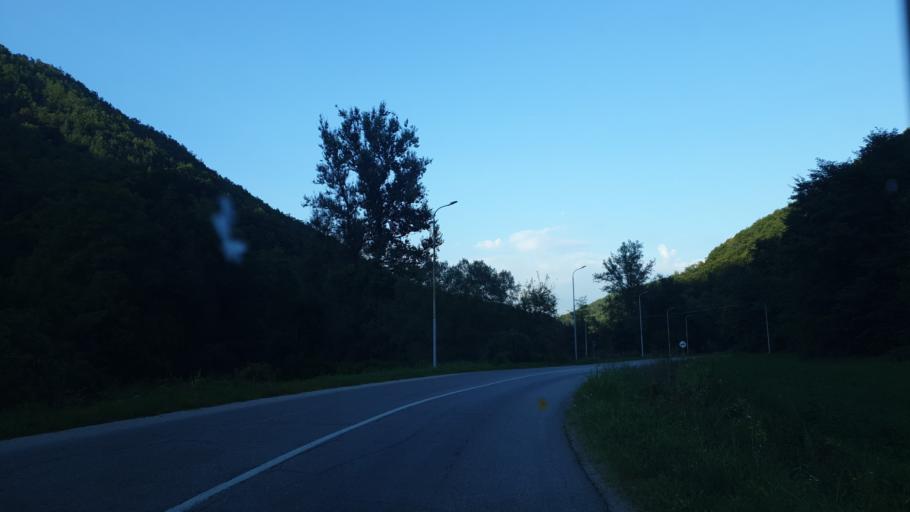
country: RS
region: Central Serbia
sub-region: Zlatiborski Okrug
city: Pozega
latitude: 43.9334
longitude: 20.0019
